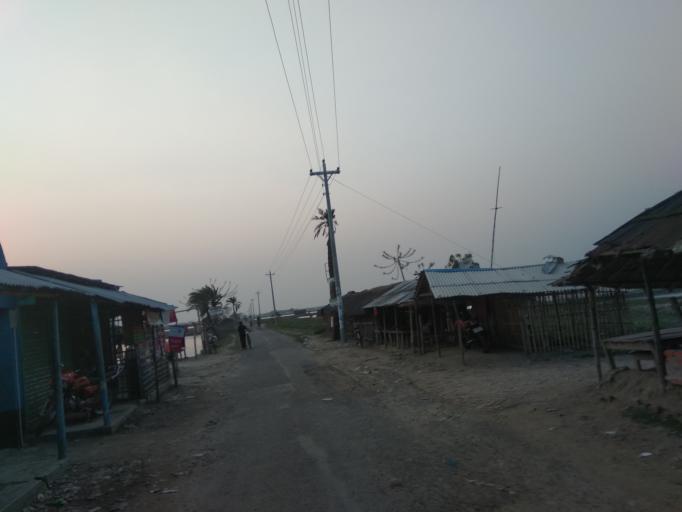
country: IN
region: West Bengal
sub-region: North 24 Parganas
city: Taki
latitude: 22.4567
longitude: 89.0730
